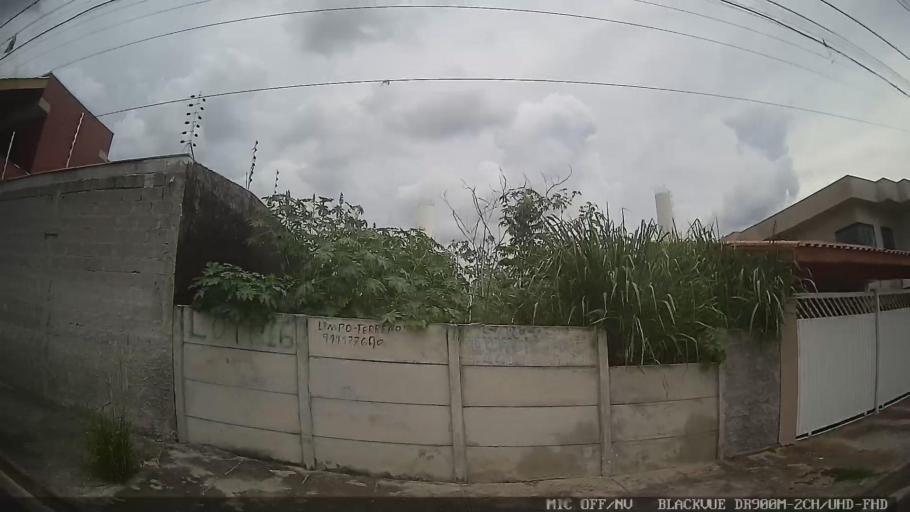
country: BR
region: Sao Paulo
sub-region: Atibaia
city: Atibaia
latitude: -23.1313
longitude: -46.5973
